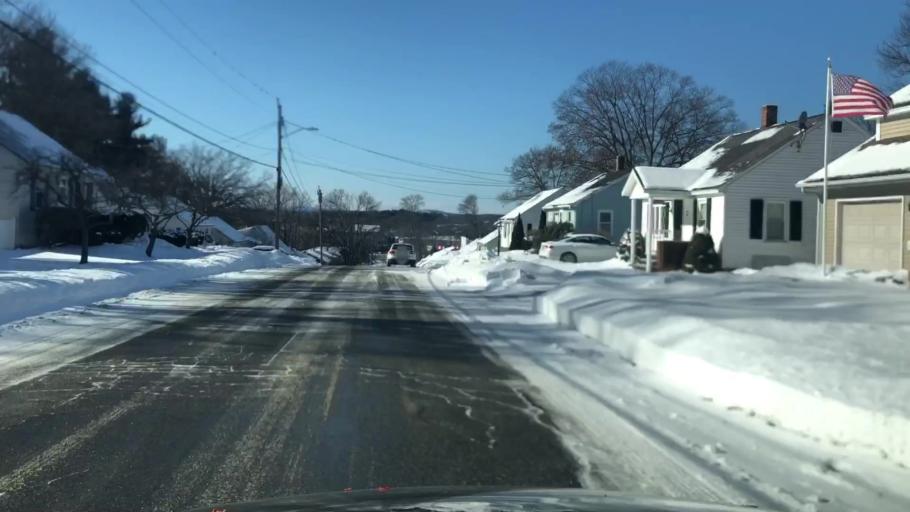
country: US
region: New Hampshire
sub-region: Hillsborough County
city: Manchester
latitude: 42.9665
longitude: -71.4451
